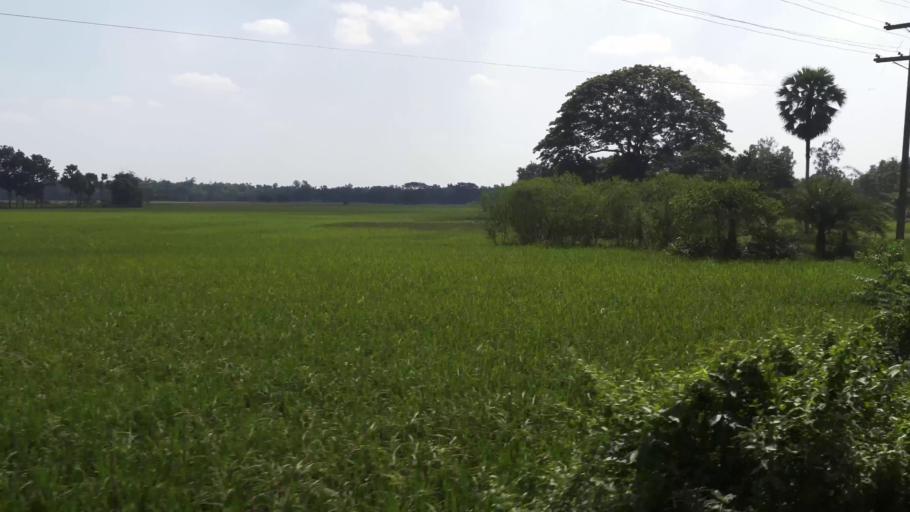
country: BD
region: Dhaka
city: Gafargaon
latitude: 24.2271
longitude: 90.4881
